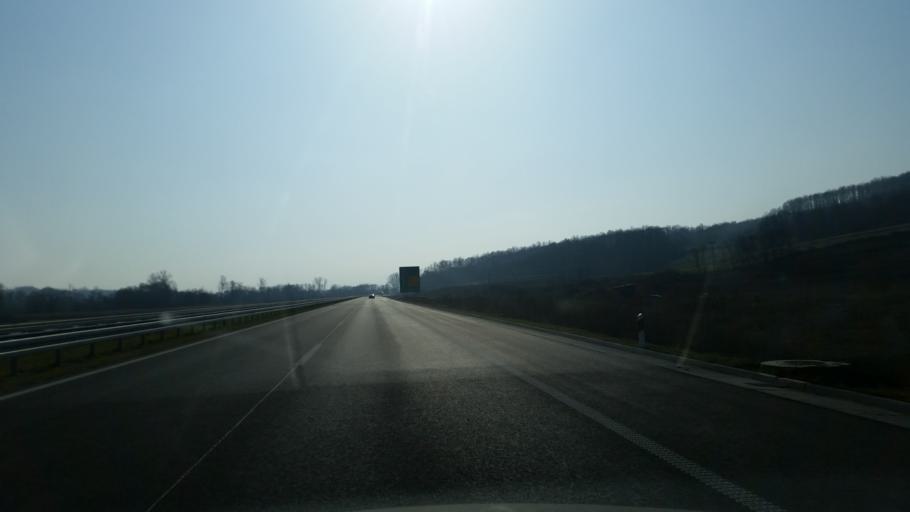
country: RS
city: Prislonica
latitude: 43.9359
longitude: 20.4008
